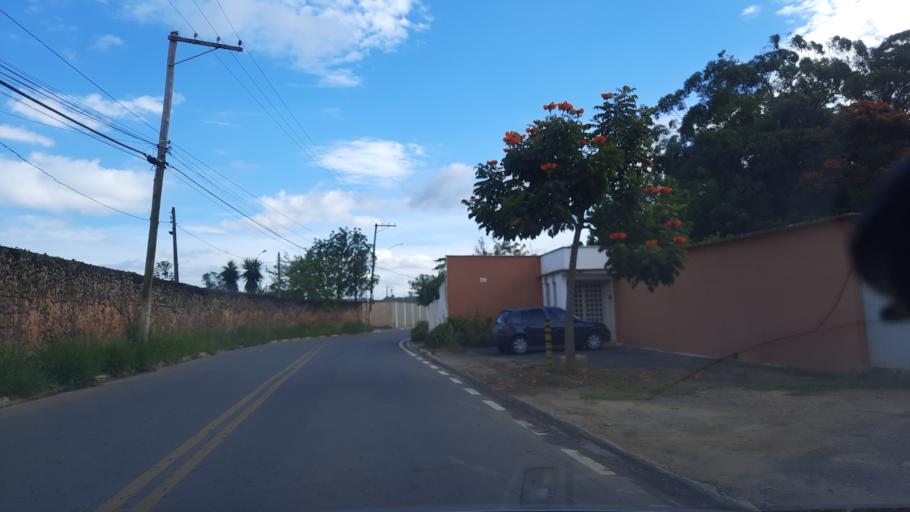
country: BR
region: Sao Paulo
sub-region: Atibaia
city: Atibaia
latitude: -23.1036
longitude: -46.5227
